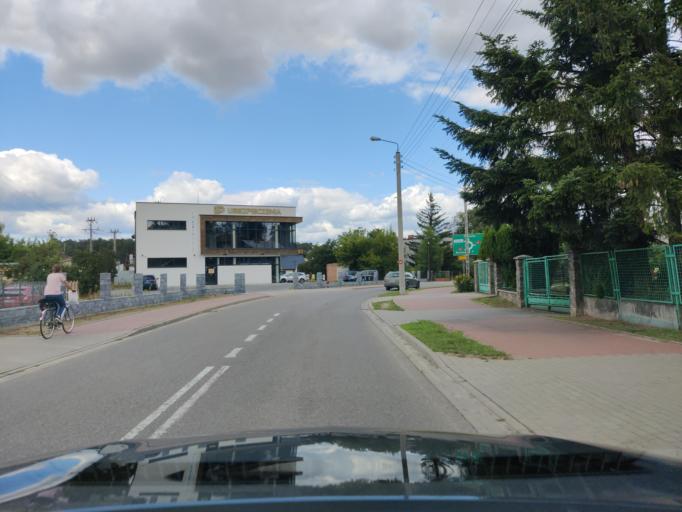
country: PL
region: Masovian Voivodeship
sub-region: Powiat wegrowski
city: Wegrow
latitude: 52.4030
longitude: 22.0207
